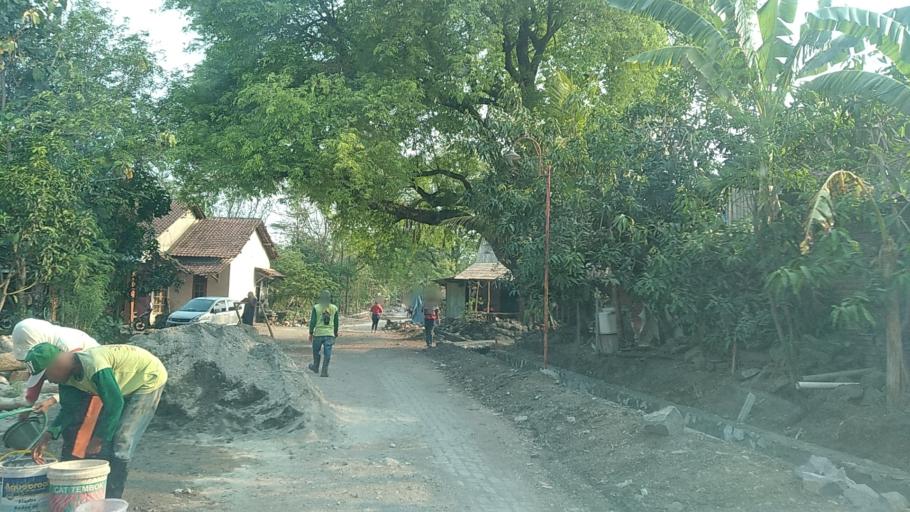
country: ID
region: Central Java
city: Mranggen
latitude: -7.0640
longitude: 110.4858
